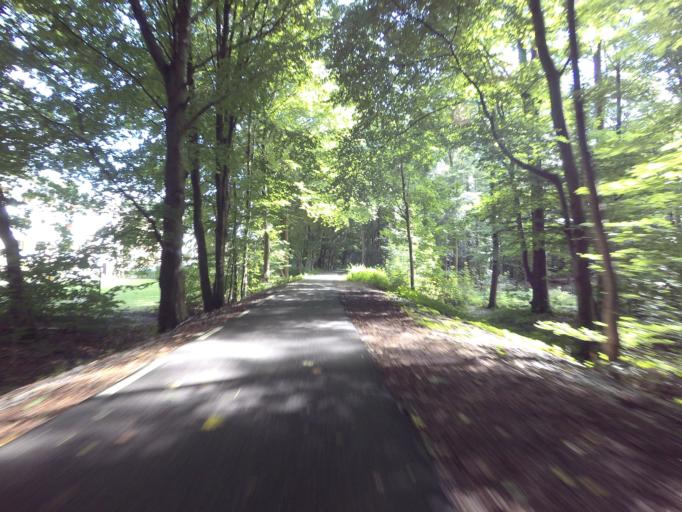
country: DK
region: Central Jutland
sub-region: Silkeborg Kommune
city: Silkeborg
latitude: 56.1673
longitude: 9.5689
